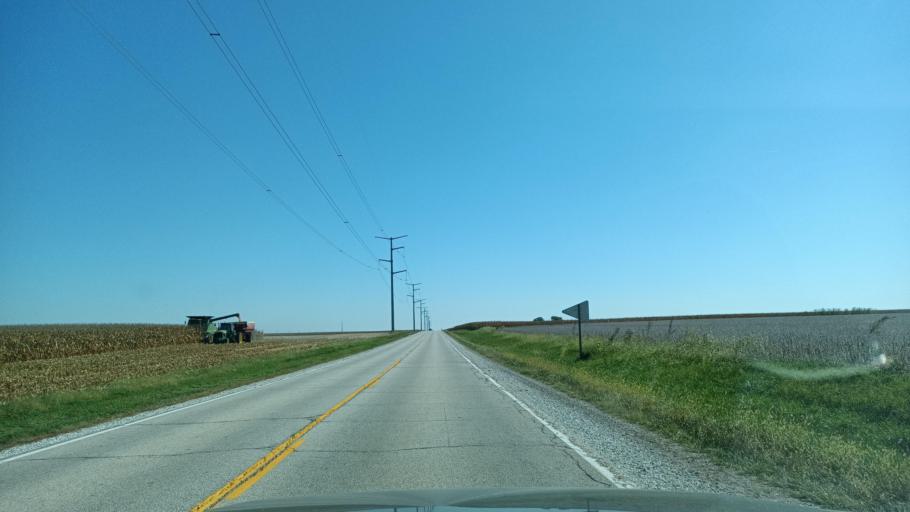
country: US
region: Illinois
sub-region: Peoria County
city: Elmwood
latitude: 40.9023
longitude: -89.9972
